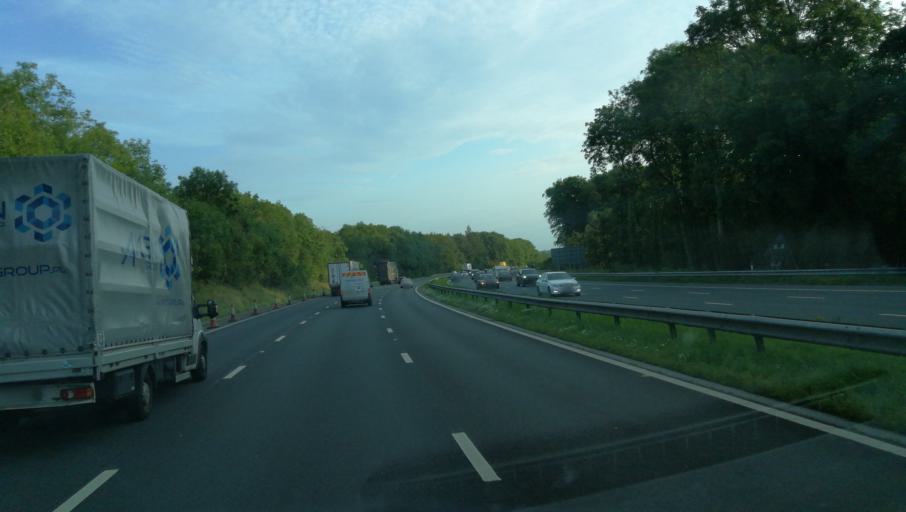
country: GB
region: England
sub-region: Lancashire
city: Bolton le Sands
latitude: 54.0857
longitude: -2.7664
